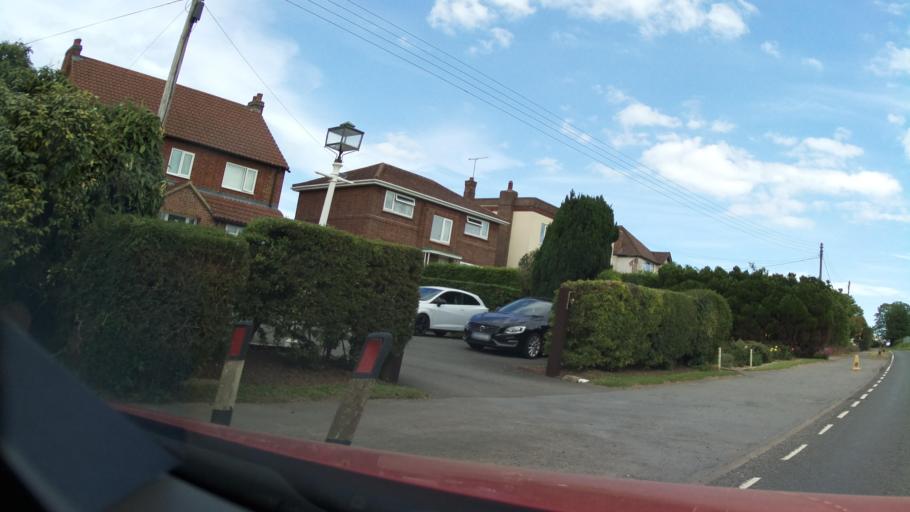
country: GB
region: England
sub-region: Worcestershire
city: Kempsey
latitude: 52.1656
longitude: -2.1751
